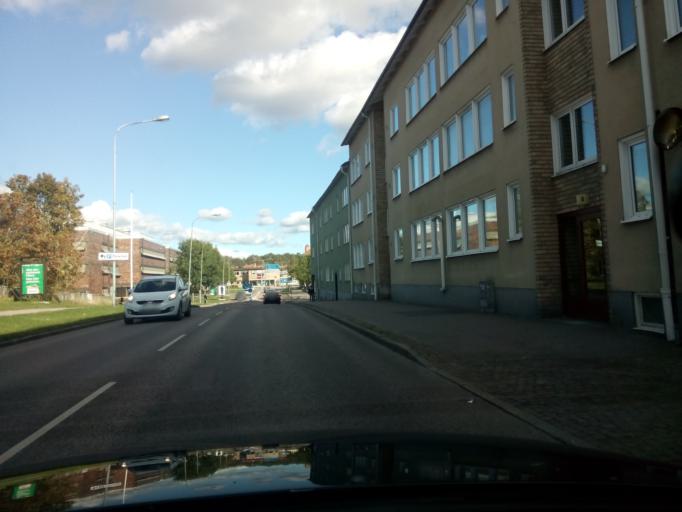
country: SE
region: Soedermanland
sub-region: Nykopings Kommun
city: Nykoping
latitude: 58.7564
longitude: 17.0132
